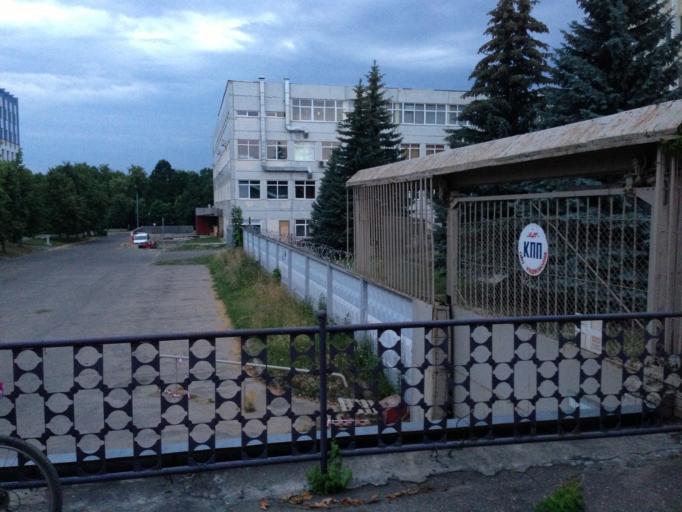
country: BY
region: Grodnenskaya
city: Hrodna
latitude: 53.7034
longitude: 23.8201
